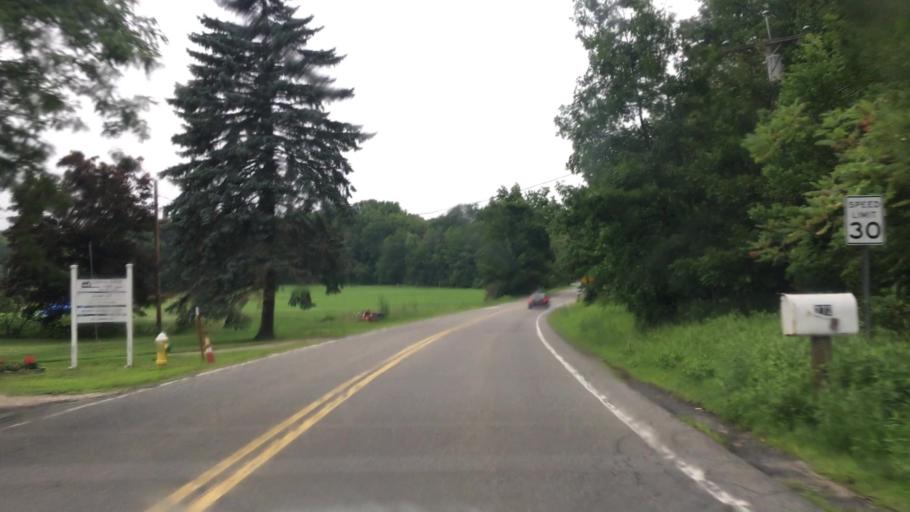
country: US
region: Maine
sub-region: York County
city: South Eliot
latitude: 43.1000
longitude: -70.8328
